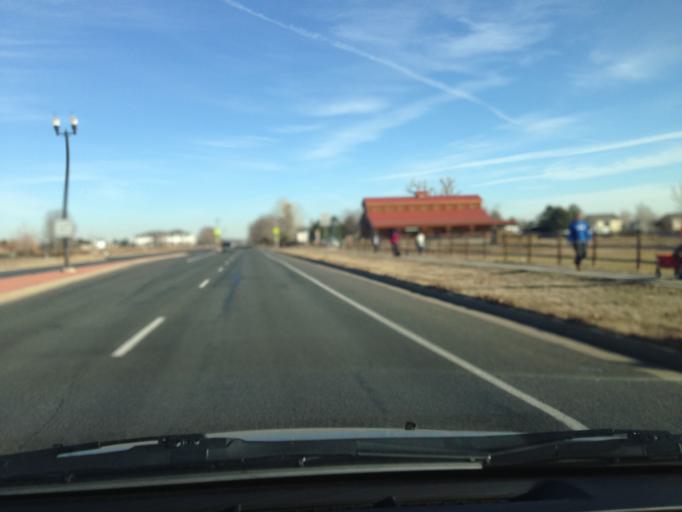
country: US
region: Colorado
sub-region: Boulder County
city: Lafayette
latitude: 40.0001
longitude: -105.1111
